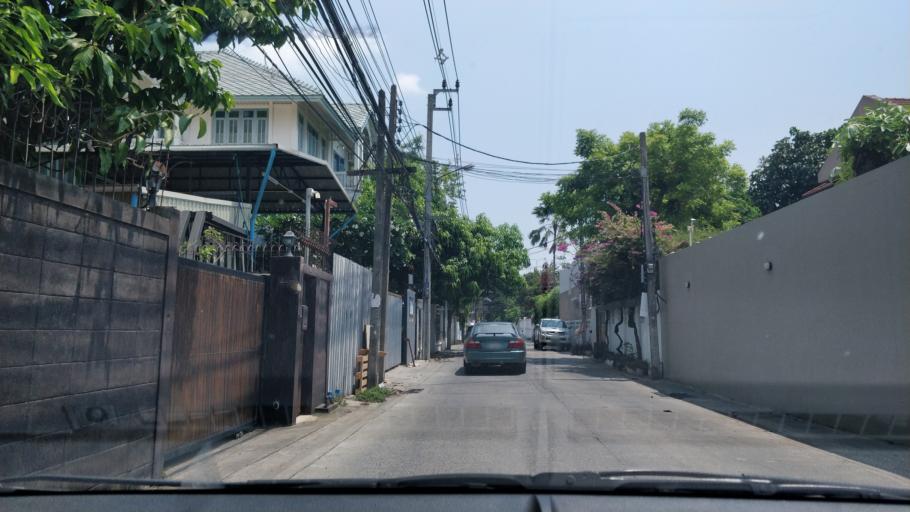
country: TH
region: Bangkok
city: Watthana
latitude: 13.7232
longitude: 100.6037
